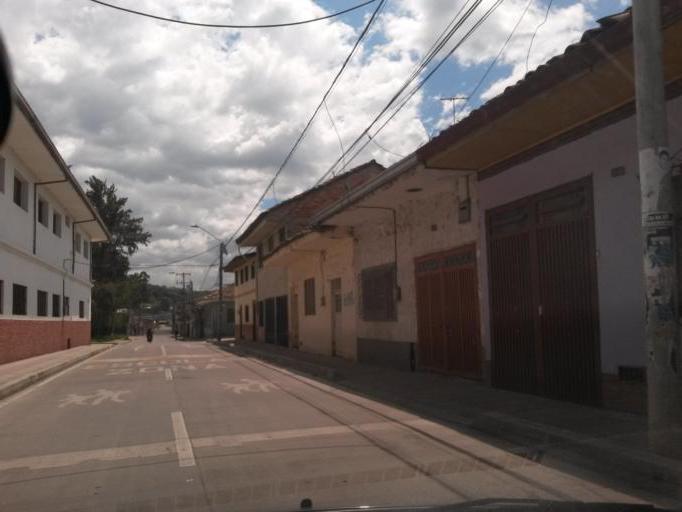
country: CO
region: Cauca
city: Popayan
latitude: 2.4353
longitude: -76.6062
